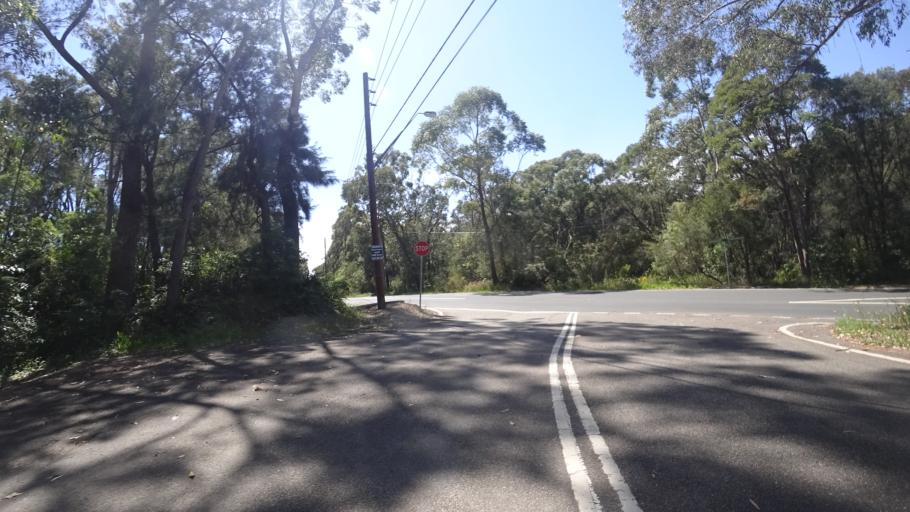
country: AU
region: New South Wales
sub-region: City of Sydney
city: North Turramurra
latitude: -33.6726
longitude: 151.1891
